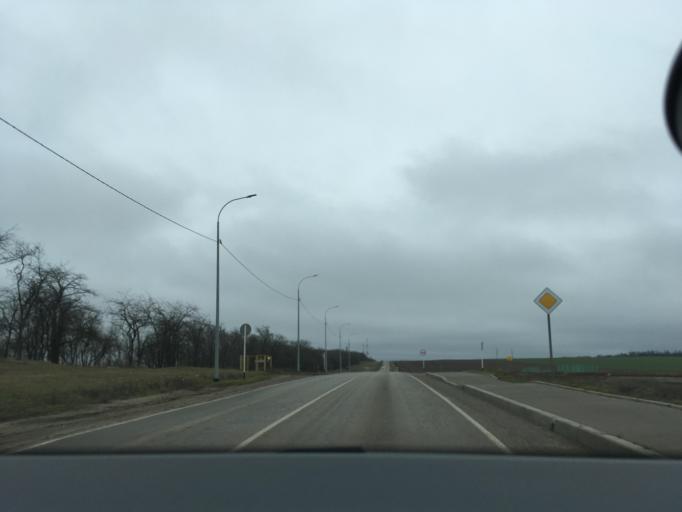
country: RU
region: Krasnodarskiy
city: Kushchevskaya
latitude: 46.5854
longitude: 39.6416
